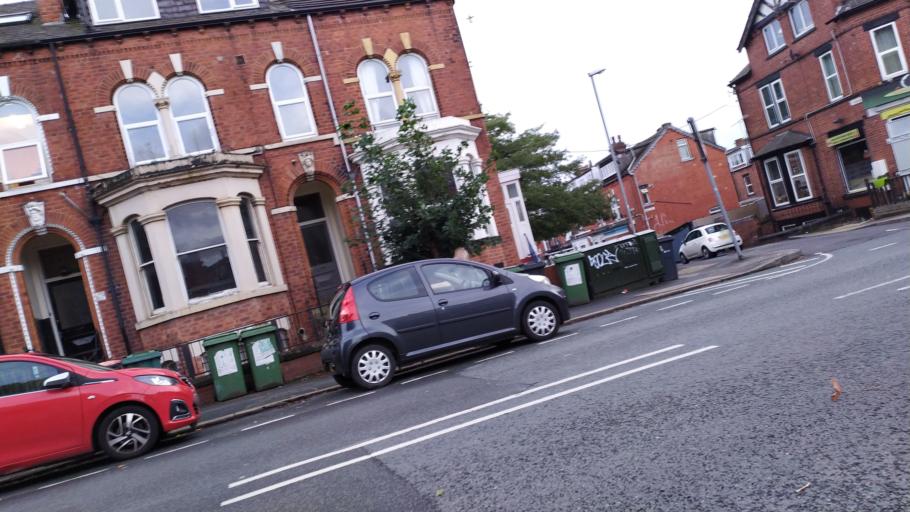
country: GB
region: England
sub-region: City and Borough of Leeds
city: Leeds
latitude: 53.8144
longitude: -1.5740
